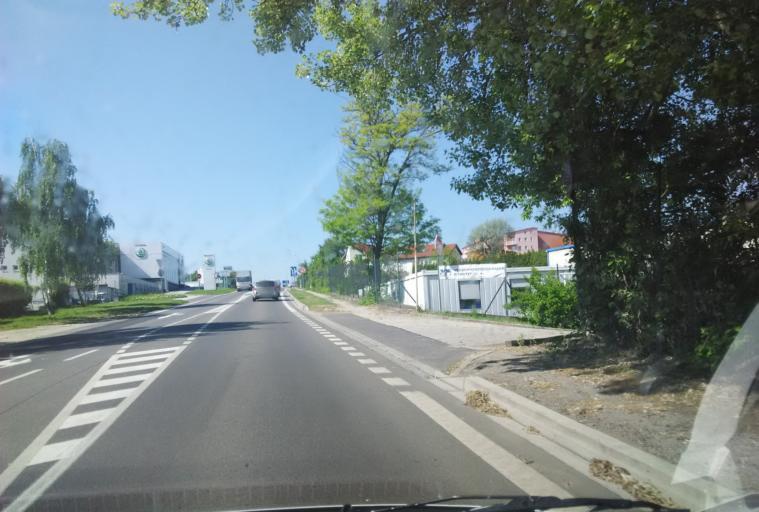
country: SK
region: Nitriansky
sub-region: Okres Nitra
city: Nitra
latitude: 48.2886
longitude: 18.0747
